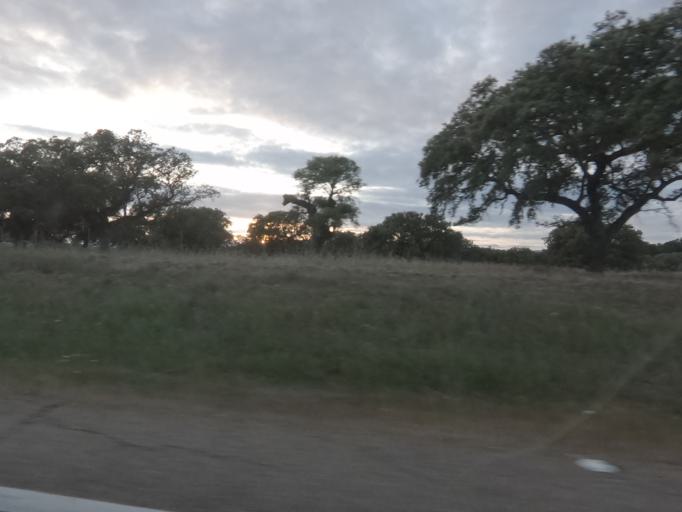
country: ES
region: Extremadura
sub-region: Provincia de Badajoz
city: Villar del Rey
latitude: 39.0429
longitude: -6.8084
